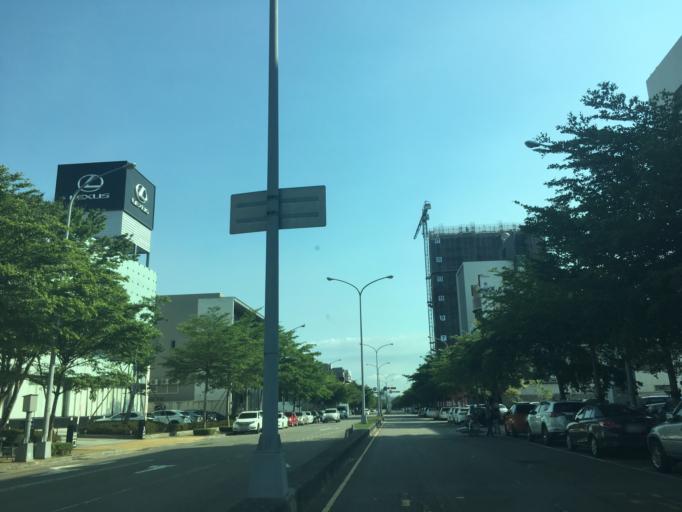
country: TW
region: Taiwan
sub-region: Taichung City
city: Taichung
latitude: 24.1589
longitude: 120.6293
